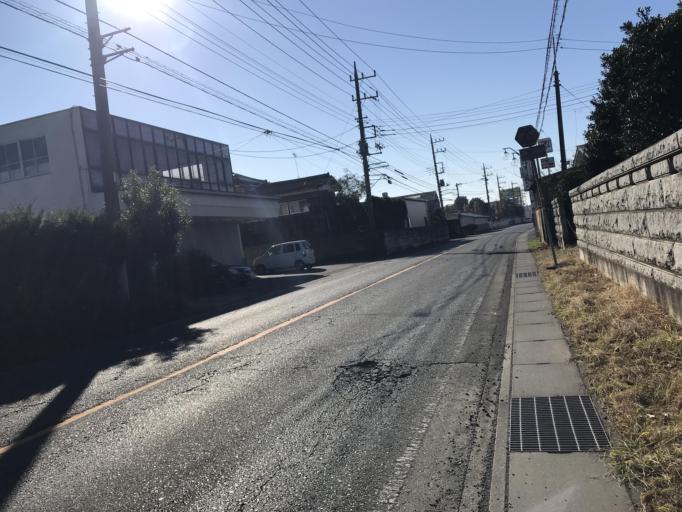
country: JP
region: Ibaraki
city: Sakai
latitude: 36.1908
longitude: 139.8113
